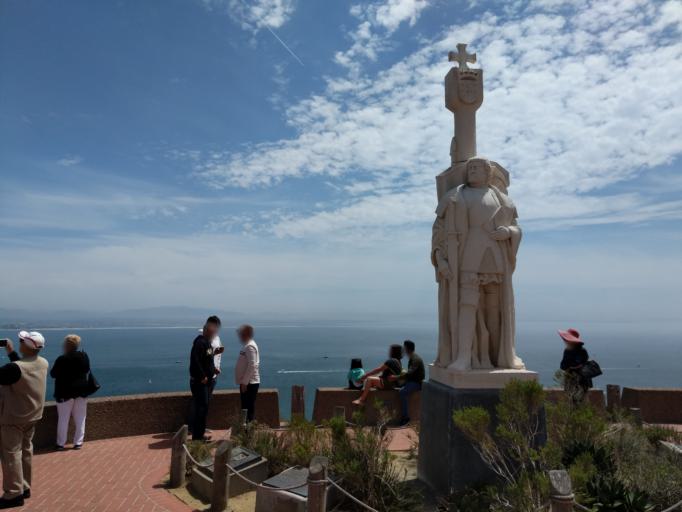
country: US
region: California
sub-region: San Diego County
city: Coronado
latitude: 32.6740
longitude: -117.2390
